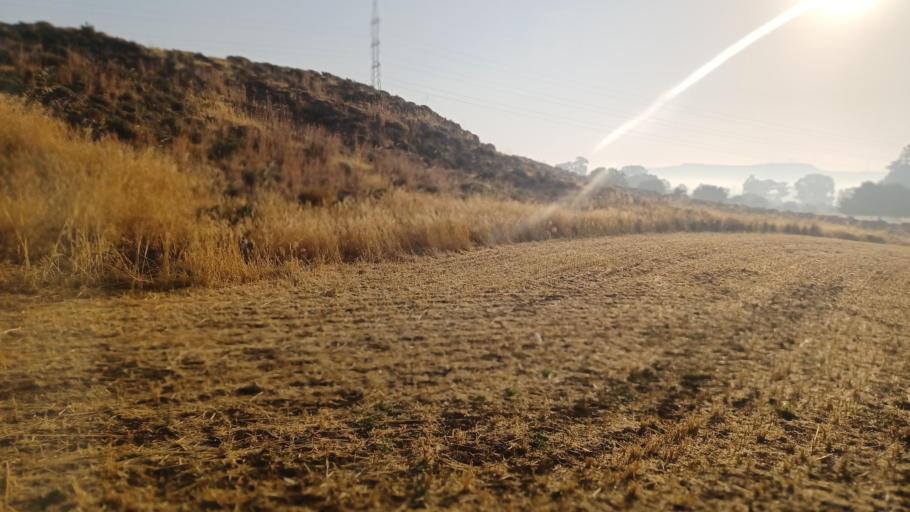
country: CY
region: Larnaka
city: Mosfiloti
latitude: 34.9740
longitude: 33.4318
